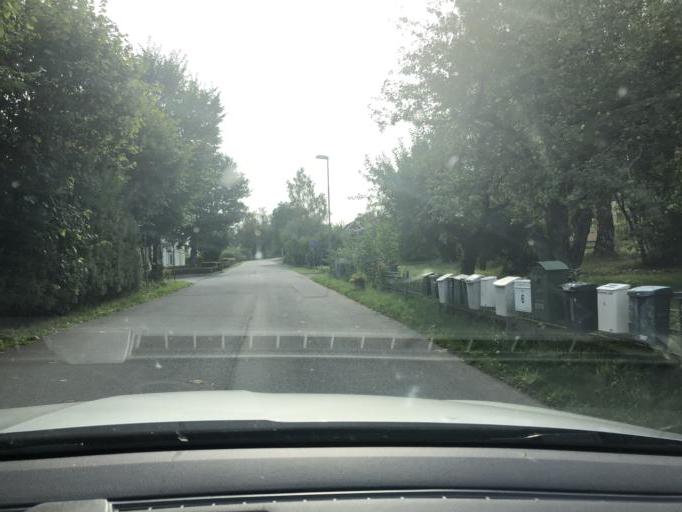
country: SE
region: Joenkoeping
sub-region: Vetlanda Kommun
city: Ekenassjon
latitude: 57.5200
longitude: 14.9090
